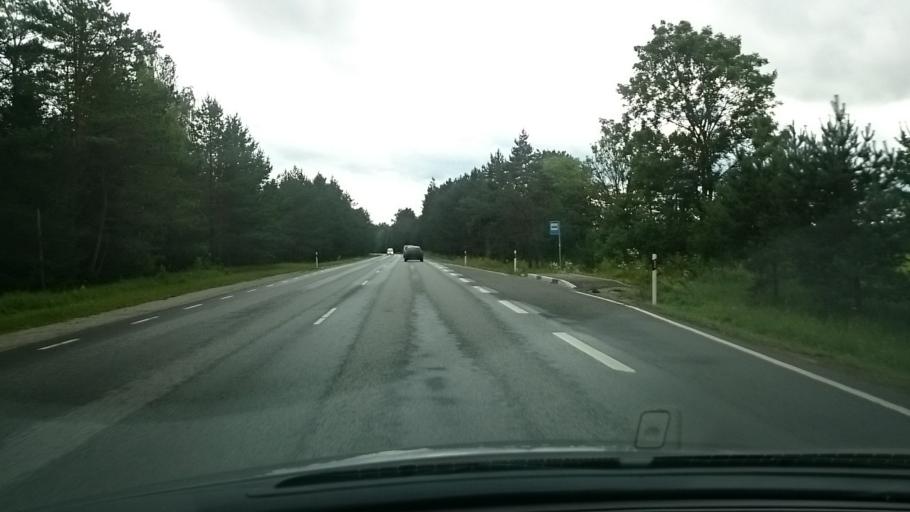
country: EE
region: Harju
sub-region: Keila linn
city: Keila
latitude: 59.2531
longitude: 24.2836
